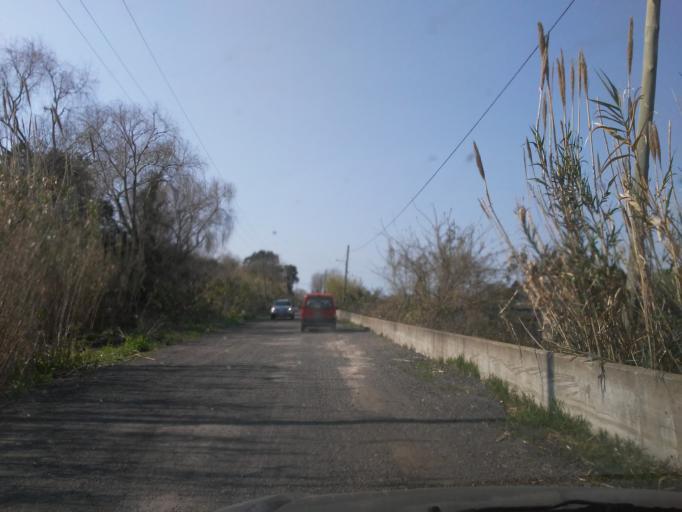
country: AR
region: Buenos Aires
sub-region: Partido de Avellaneda
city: Avellaneda
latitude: -34.6732
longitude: -58.3069
